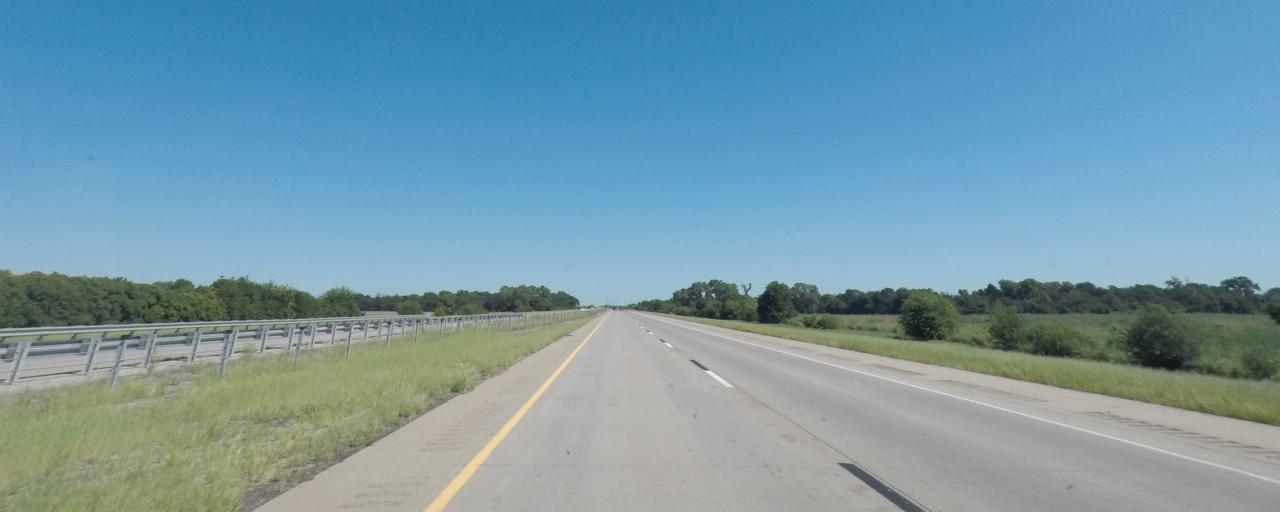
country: US
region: Oklahoma
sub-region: Noble County
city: Perry
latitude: 36.4709
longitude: -97.3269
